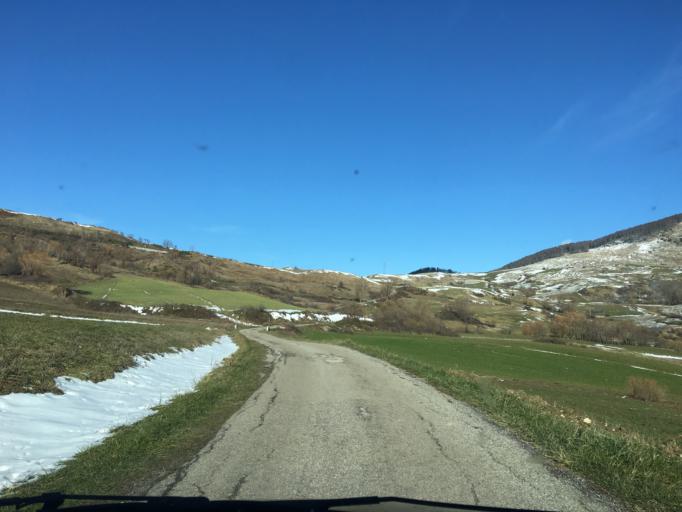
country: IT
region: Molise
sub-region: Provincia di Isernia
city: Agnone
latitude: 41.8479
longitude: 14.3529
